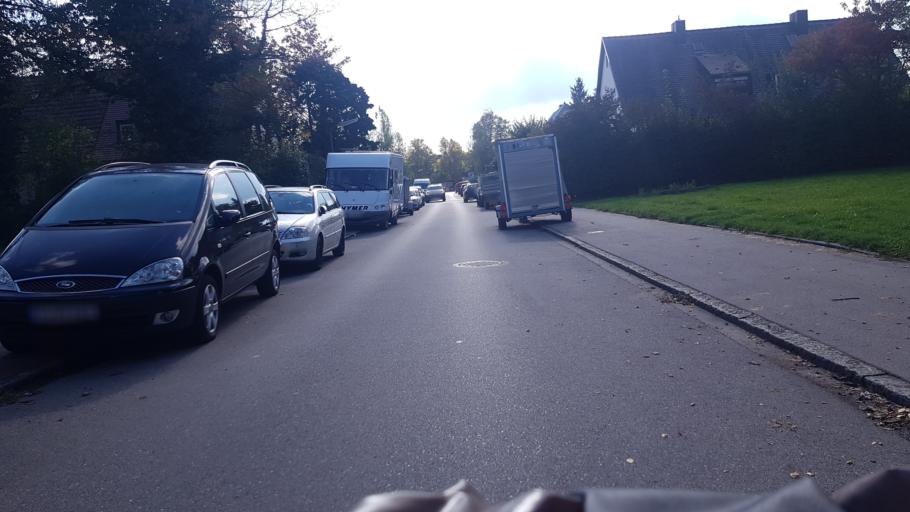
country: DE
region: Bavaria
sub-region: Upper Bavaria
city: Pasing
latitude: 48.1315
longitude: 11.4894
